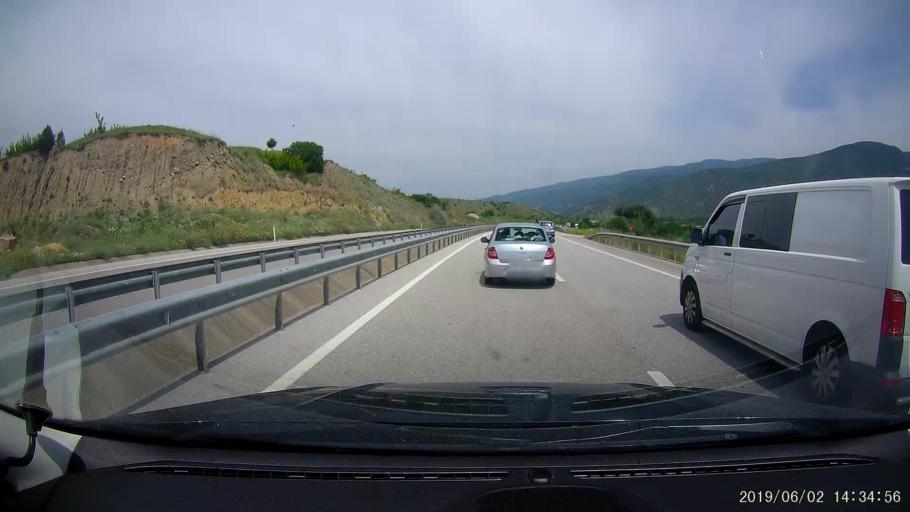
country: TR
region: Kastamonu
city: Tosya
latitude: 41.0408
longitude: 34.2042
